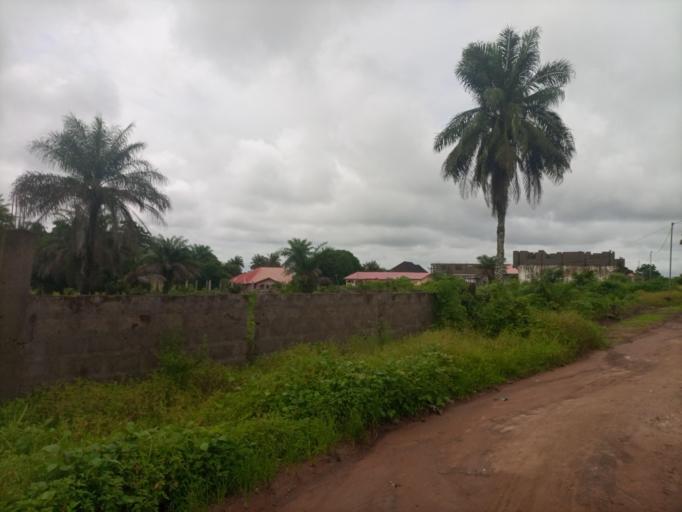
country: SL
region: Northern Province
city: Masoyila
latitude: 8.5949
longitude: -13.1760
